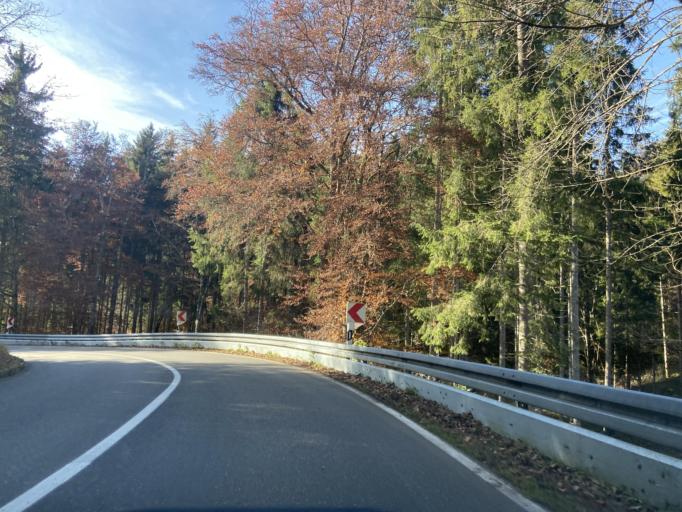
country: DE
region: Baden-Wuerttemberg
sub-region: Tuebingen Region
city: Stetten am Kalten Markt
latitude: 48.1110
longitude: 9.0884
